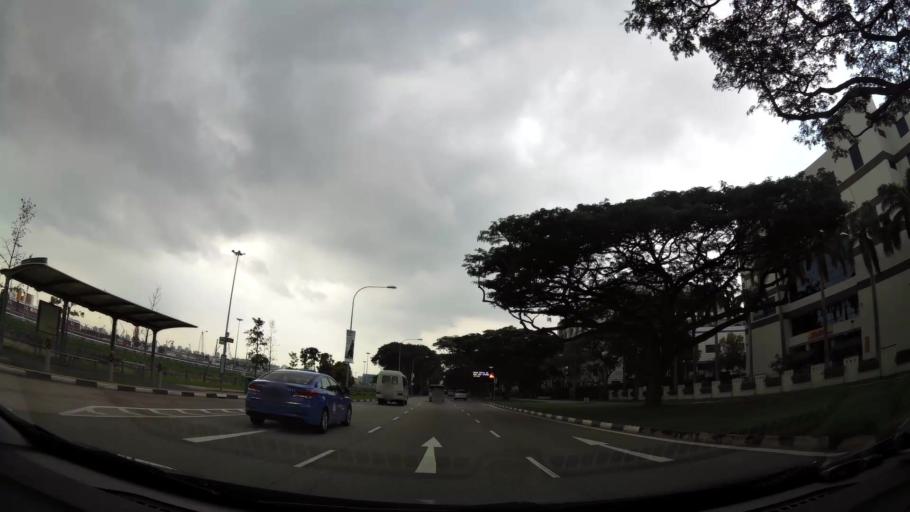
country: SG
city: Singapore
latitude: 1.3293
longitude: 103.9636
